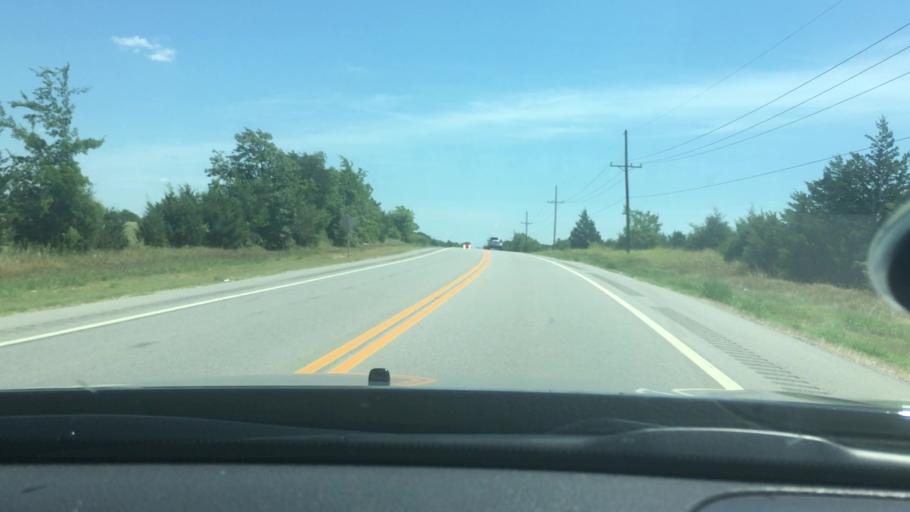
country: US
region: Oklahoma
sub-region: Bryan County
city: Durant
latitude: 33.9989
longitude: -96.2215
